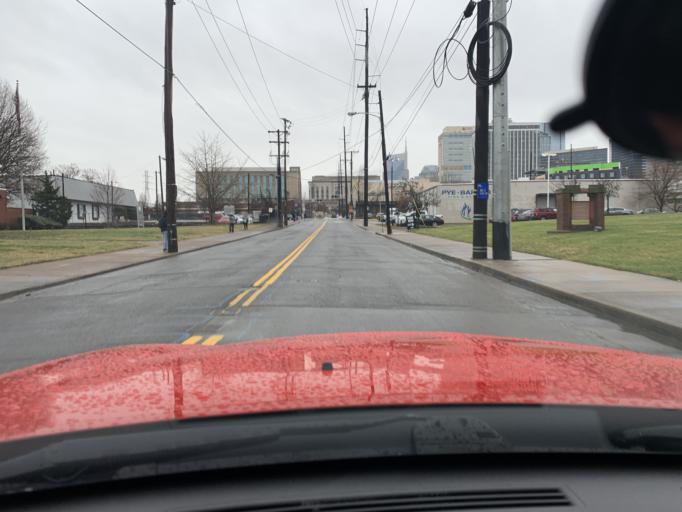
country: US
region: Tennessee
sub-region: Davidson County
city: Nashville
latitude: 36.1718
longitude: -86.7814
